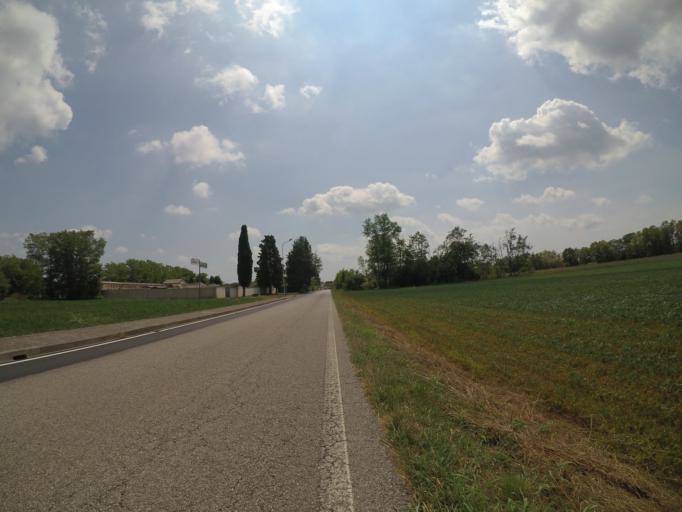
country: IT
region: Friuli Venezia Giulia
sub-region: Provincia di Udine
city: Basiliano
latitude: 45.9993
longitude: 13.0768
